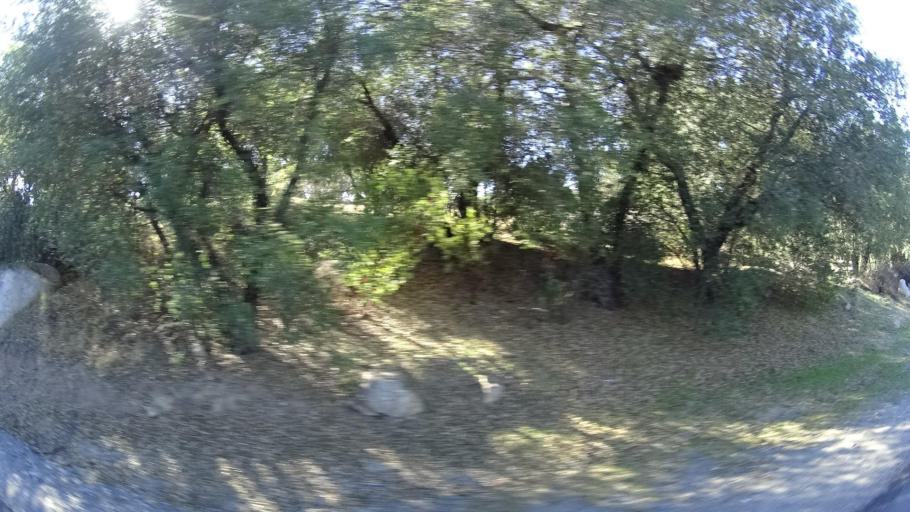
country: MX
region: Baja California
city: Tecate
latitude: 32.6763
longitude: -116.7236
